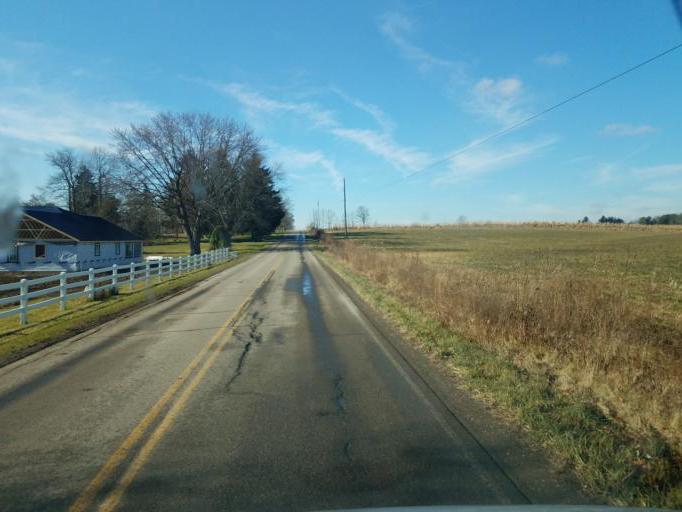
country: US
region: Ohio
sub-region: Wayne County
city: Dalton
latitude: 40.7336
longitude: -81.6787
